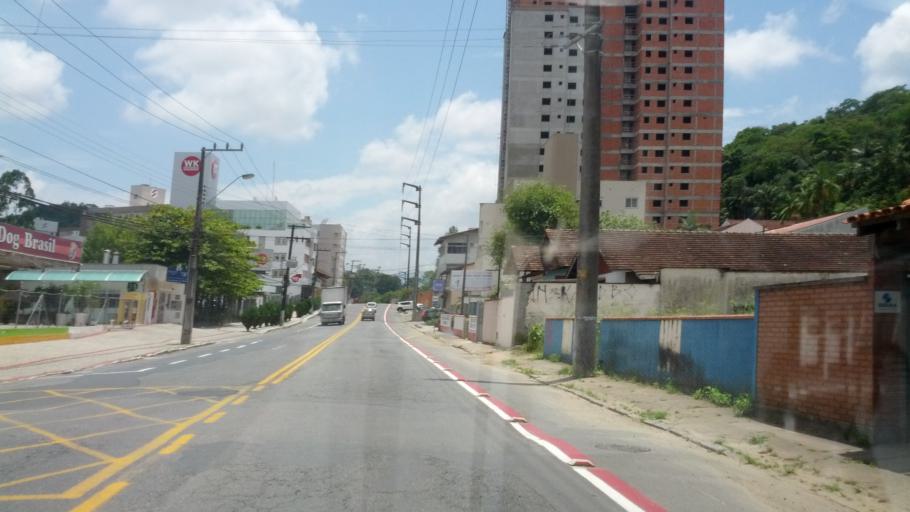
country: BR
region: Santa Catarina
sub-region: Blumenau
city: Blumenau
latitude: -26.9011
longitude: -49.0886
